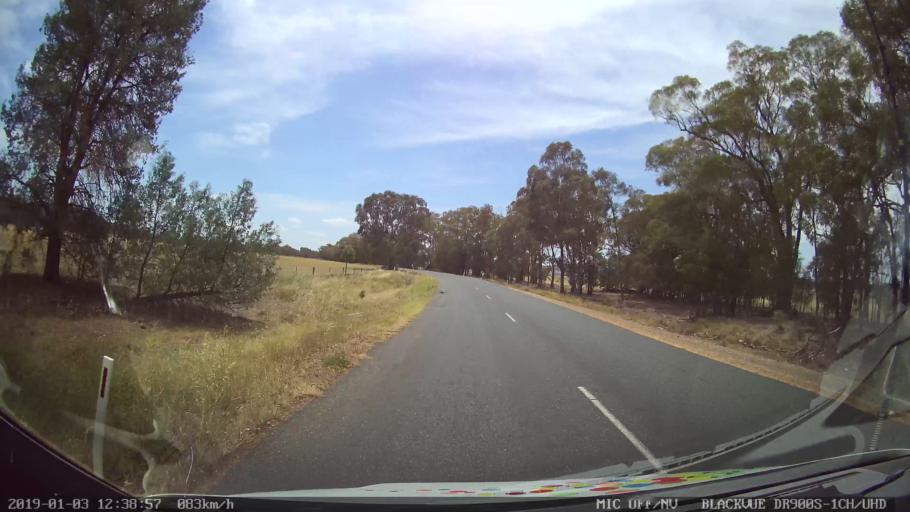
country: AU
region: New South Wales
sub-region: Weddin
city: Grenfell
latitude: -33.8295
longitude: 148.2016
